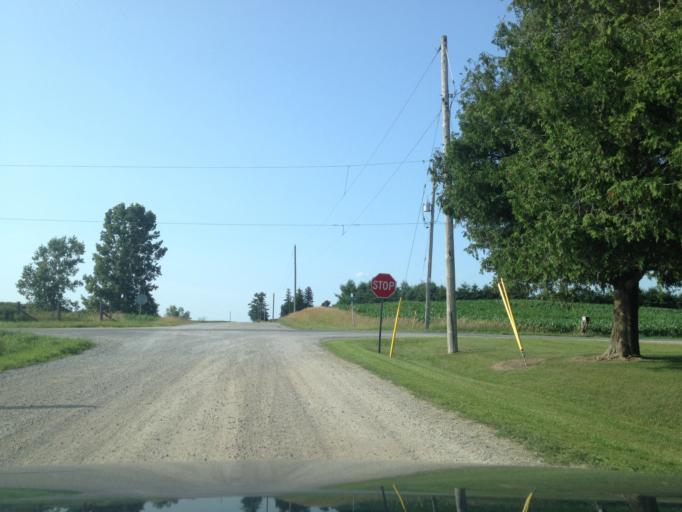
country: CA
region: Ontario
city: Ingersoll
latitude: 42.9607
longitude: -80.7750
